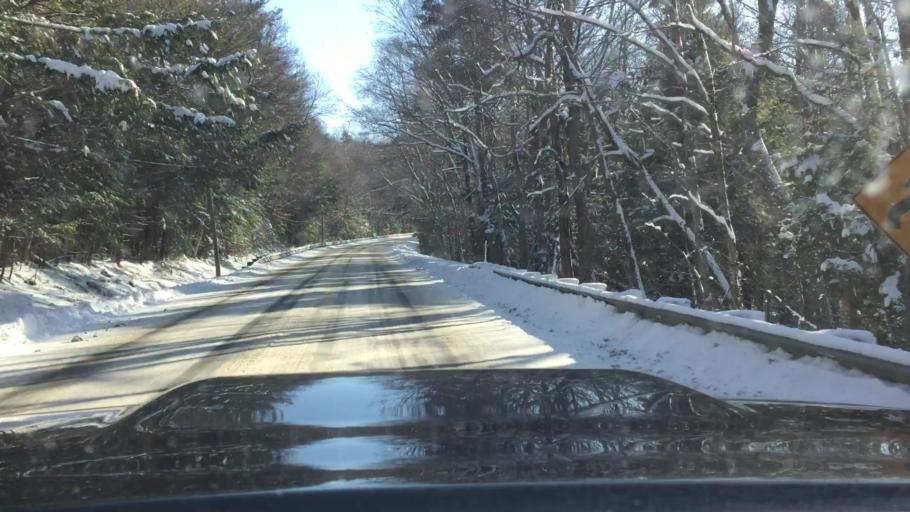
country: US
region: Massachusetts
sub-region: Berkshire County
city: Hinsdale
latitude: 42.4632
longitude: -72.9860
